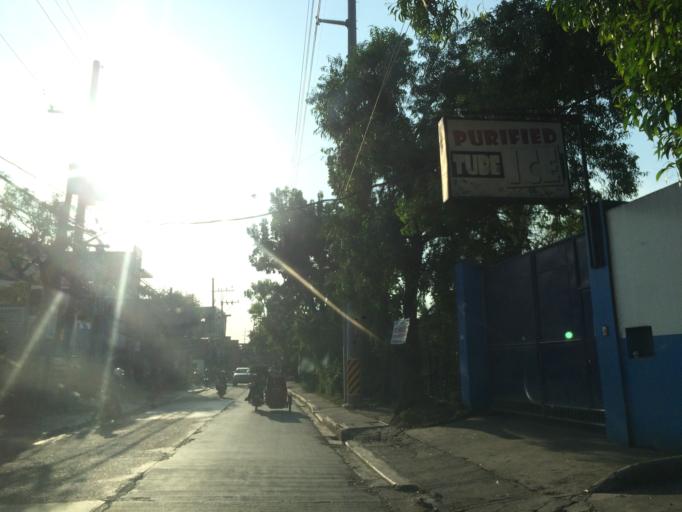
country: PH
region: Calabarzon
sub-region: Province of Rizal
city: San Mateo
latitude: 14.6811
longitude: 121.1191
